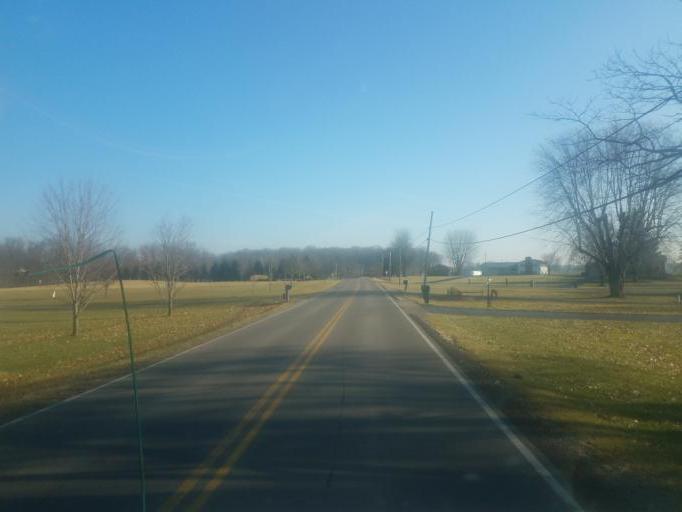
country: US
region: Ohio
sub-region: Crawford County
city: Bucyrus
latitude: 40.8213
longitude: -82.9239
